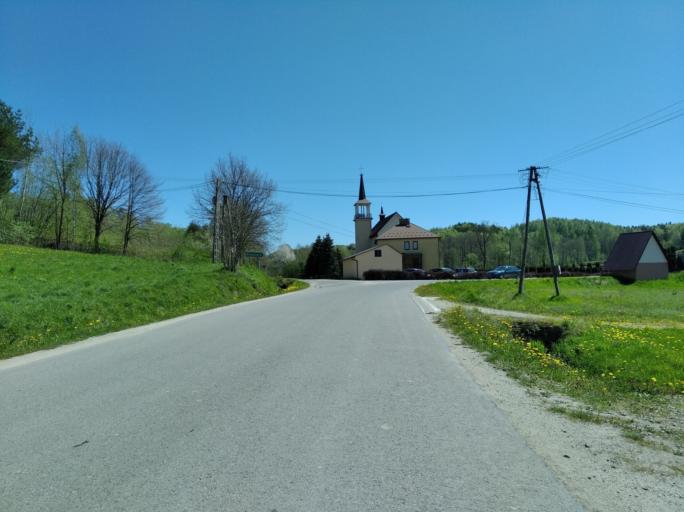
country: PL
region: Subcarpathian Voivodeship
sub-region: Powiat debicki
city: Brzostek
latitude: 49.8965
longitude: 21.4865
